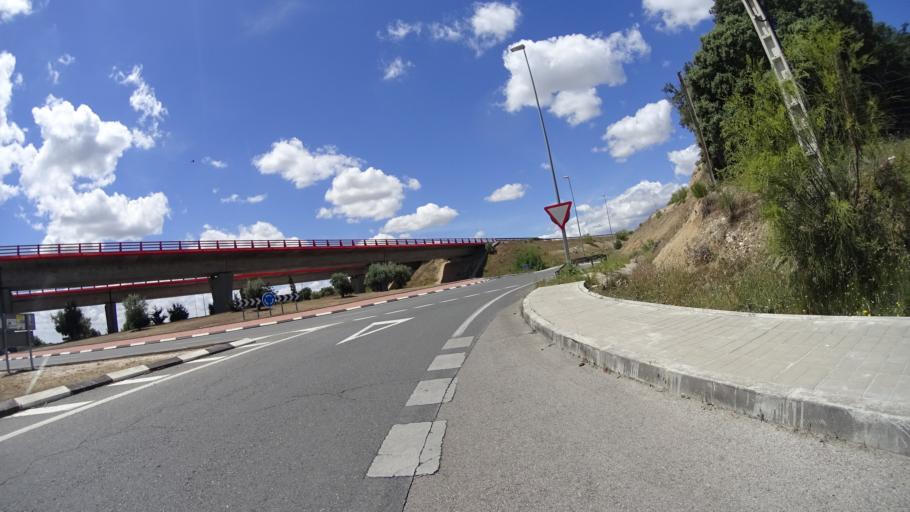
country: ES
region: Madrid
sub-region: Provincia de Madrid
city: Villanueva del Pardillo
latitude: 40.4589
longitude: -3.9469
